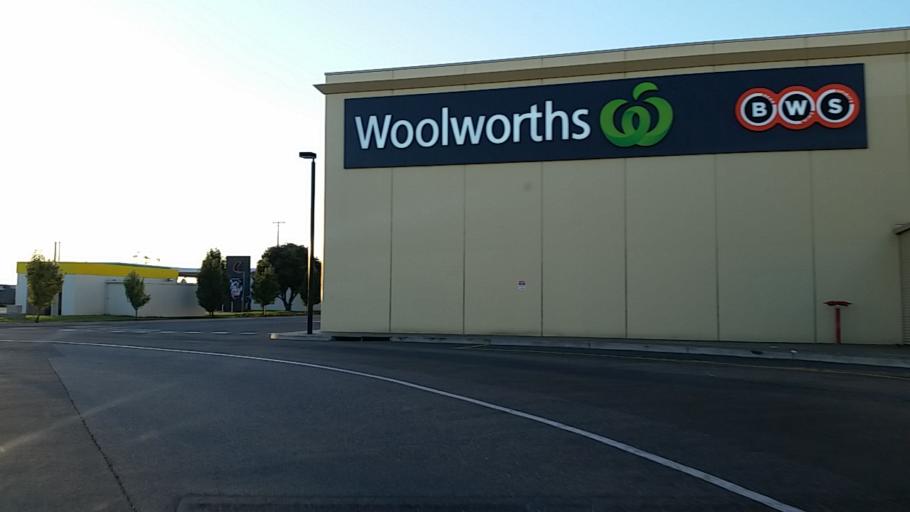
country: AU
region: South Australia
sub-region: Onkaparinga
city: Seaford
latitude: -35.1891
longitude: 138.4787
